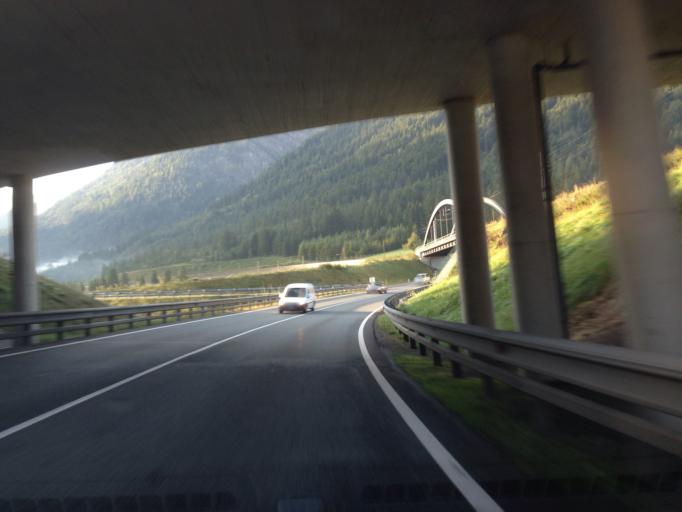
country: AT
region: Tyrol
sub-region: Politischer Bezirk Reutte
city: Heiterwang
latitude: 47.4508
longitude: 10.7332
